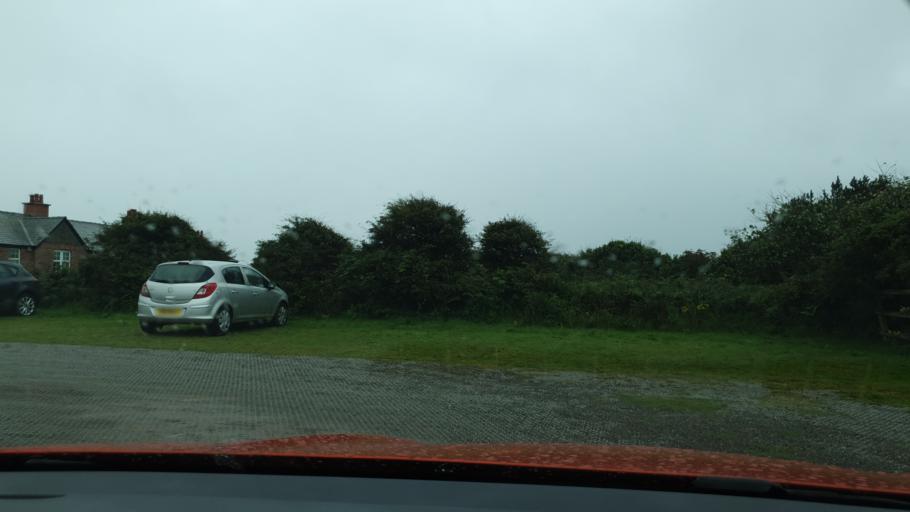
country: GB
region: England
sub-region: Cumbria
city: Barrow in Furness
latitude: 54.0489
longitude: -3.1999
